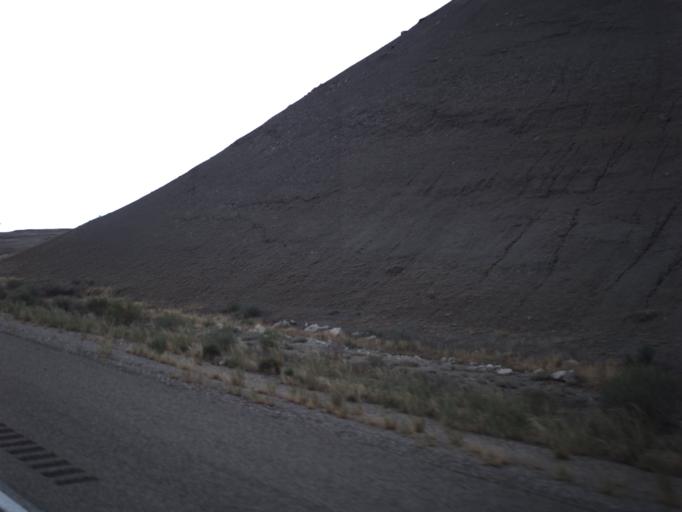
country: US
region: Utah
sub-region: Carbon County
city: East Carbon City
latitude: 38.9861
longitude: -110.1666
